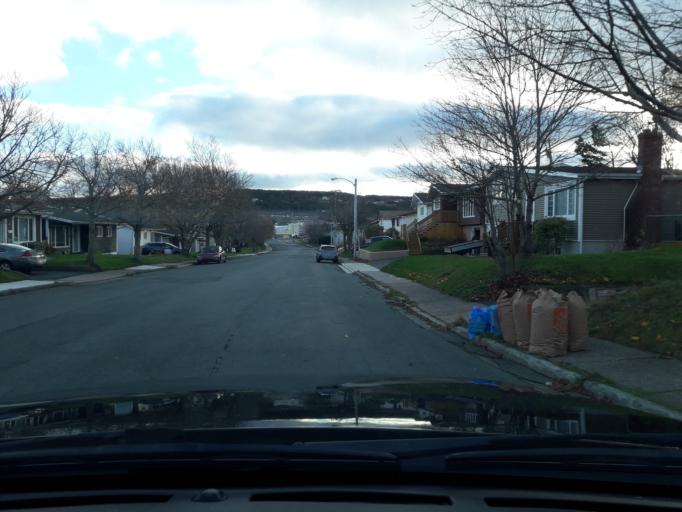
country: CA
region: Newfoundland and Labrador
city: St. John's
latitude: 47.5640
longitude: -52.7520
